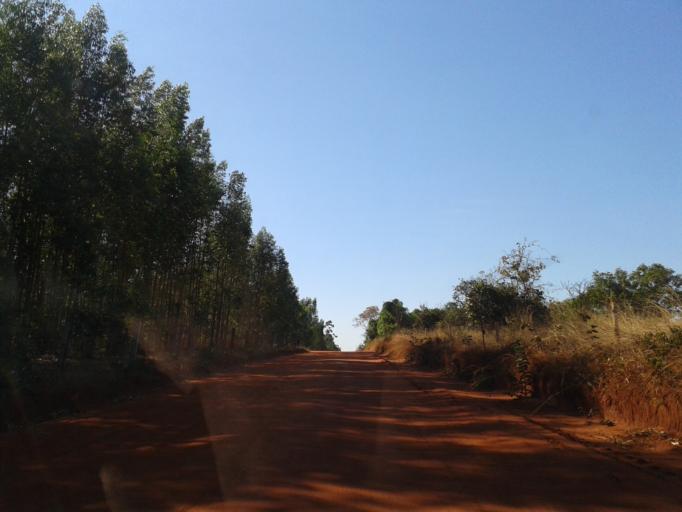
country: BR
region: Minas Gerais
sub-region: Ituiutaba
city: Ituiutaba
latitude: -19.0327
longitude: -49.3109
